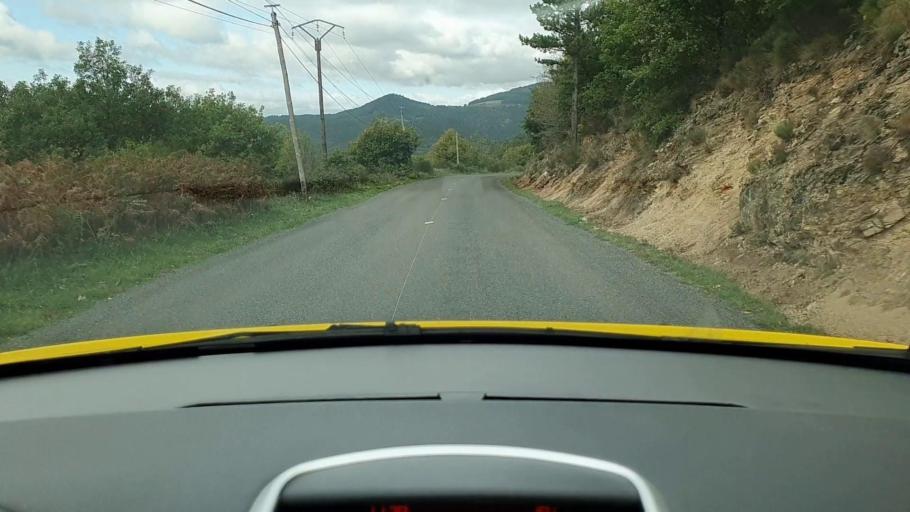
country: FR
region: Languedoc-Roussillon
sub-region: Departement de la Lozere
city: Meyrueis
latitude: 44.1060
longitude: 3.4382
